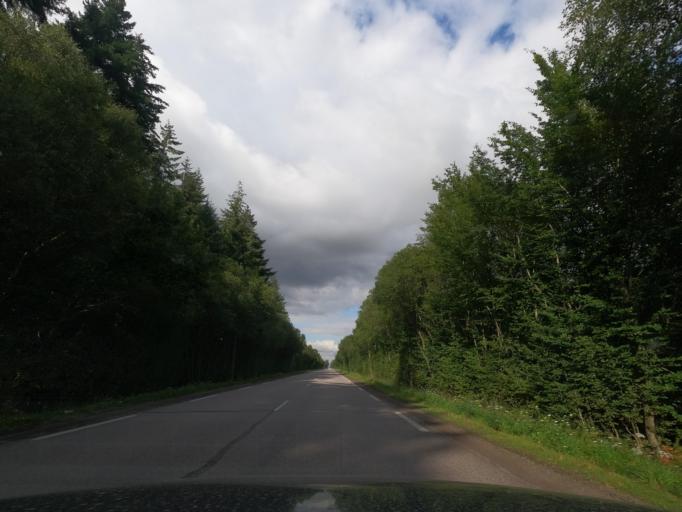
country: FR
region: Lower Normandy
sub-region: Departement de l'Orne
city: Gace
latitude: 48.8420
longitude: 0.3476
